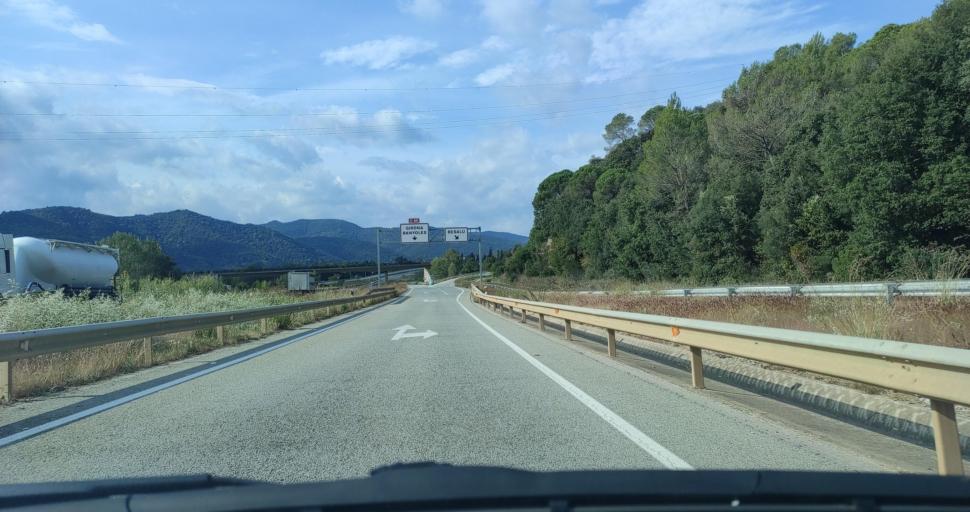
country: ES
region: Catalonia
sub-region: Provincia de Girona
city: Besalu
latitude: 42.2047
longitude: 2.7186
